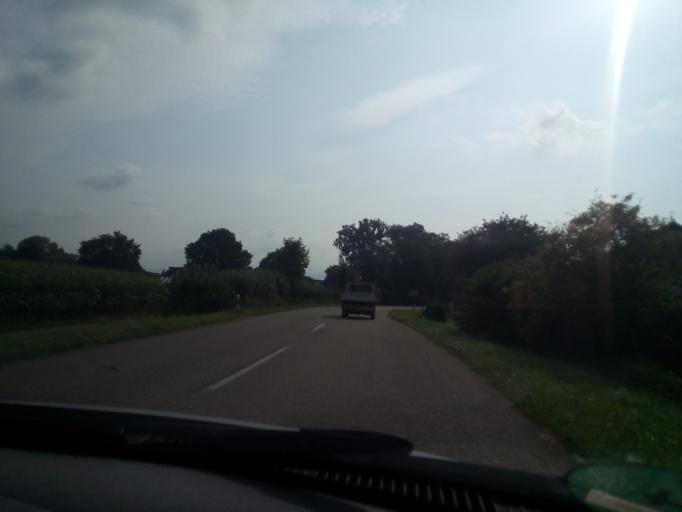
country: DE
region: Baden-Wuerttemberg
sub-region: Karlsruhe Region
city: Zell
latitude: 48.6655
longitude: 8.0141
